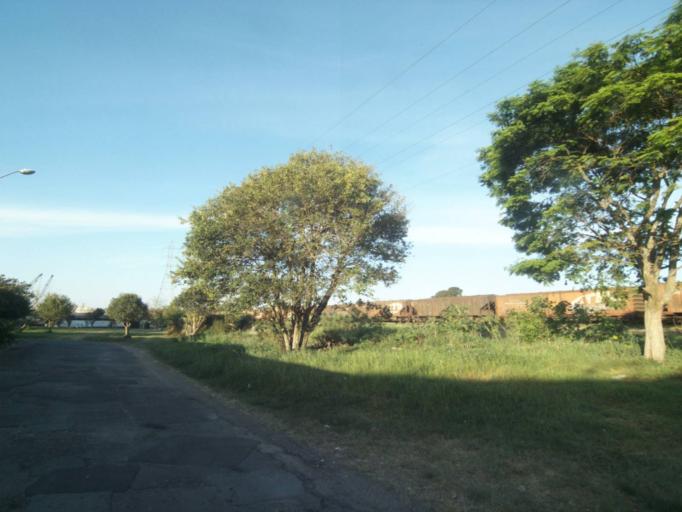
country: BR
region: Parana
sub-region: Sao Jose Dos Pinhais
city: Sao Jose dos Pinhais
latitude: -25.5224
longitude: -49.2251
